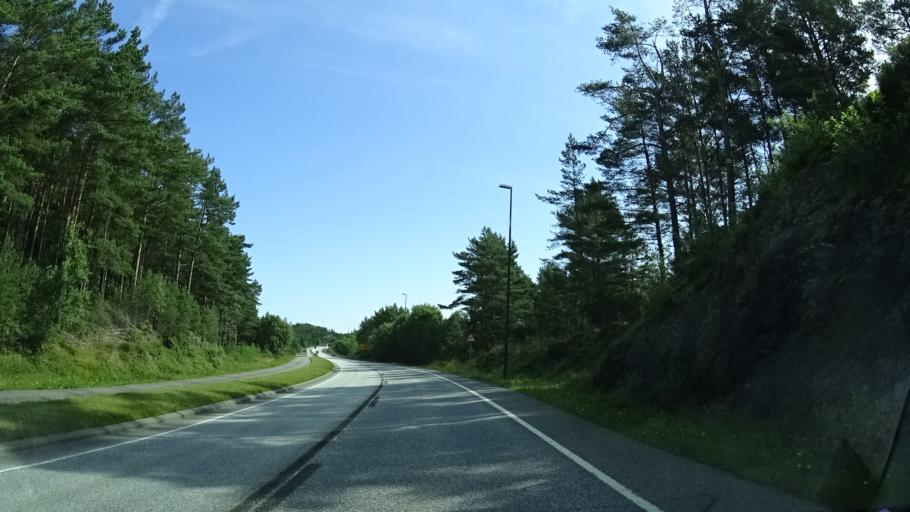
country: NO
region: Hordaland
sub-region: Bomlo
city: Mosterhamn
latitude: 59.7373
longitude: 5.3951
